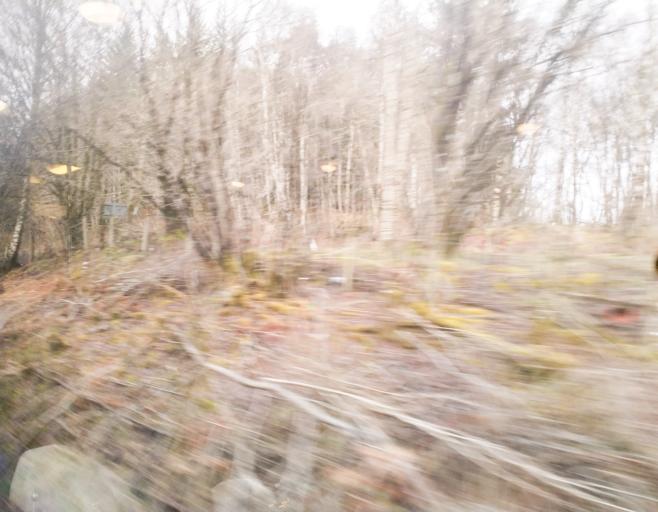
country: GB
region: Scotland
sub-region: Highland
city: Spean Bridge
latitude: 56.8912
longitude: -4.8785
